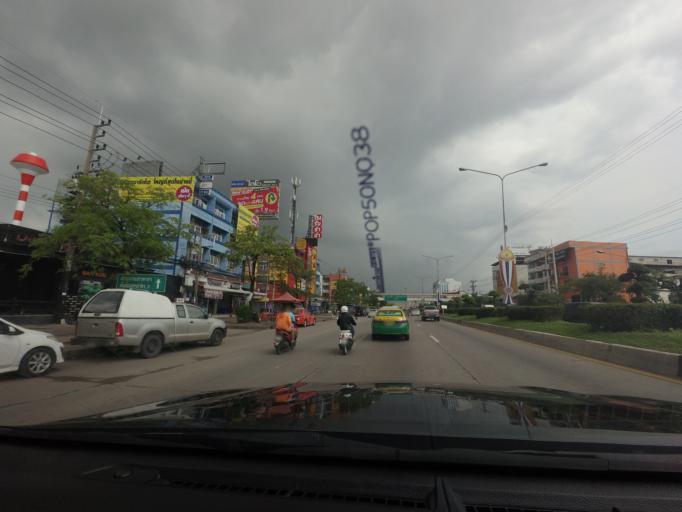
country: TH
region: Bangkok
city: Nong Khaem
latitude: 13.7046
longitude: 100.3171
